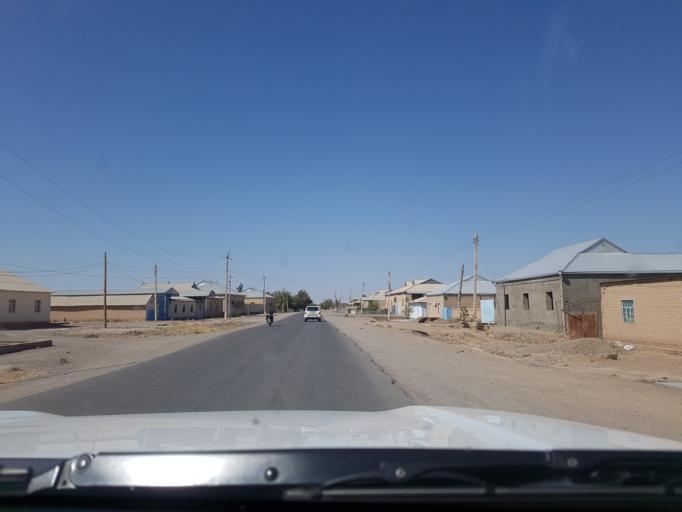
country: IR
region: Razavi Khorasan
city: Sarakhs
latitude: 36.5177
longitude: 61.2202
